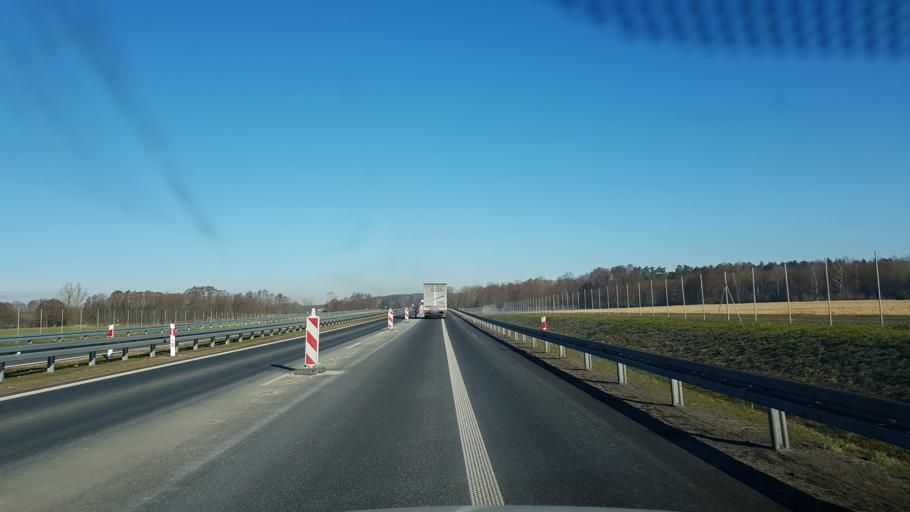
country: PL
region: West Pomeranian Voivodeship
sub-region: Powiat goleniowski
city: Przybiernow
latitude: 53.8024
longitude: 14.7746
